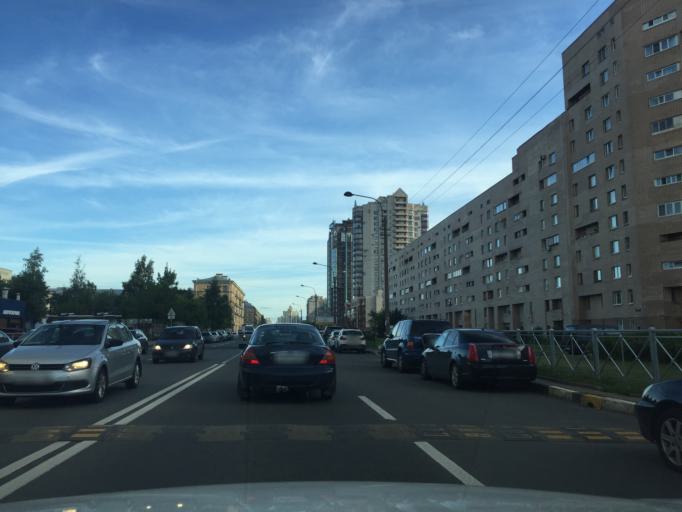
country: RU
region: St.-Petersburg
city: Kupchino
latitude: 59.8552
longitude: 30.3145
